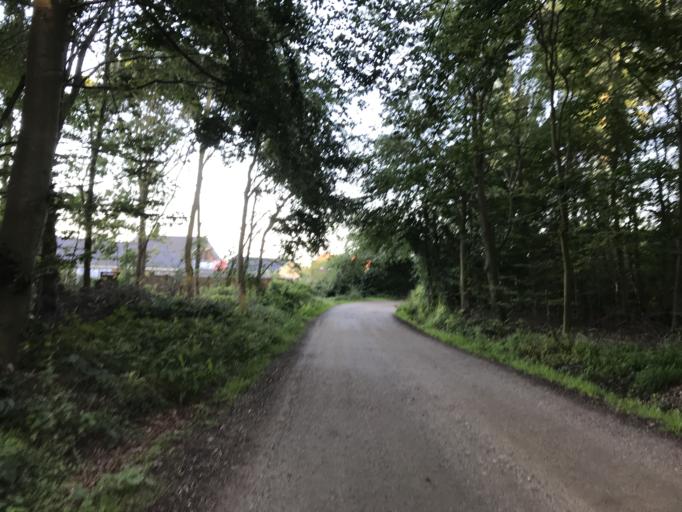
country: DK
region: South Denmark
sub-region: Middelfart Kommune
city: Middelfart
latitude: 55.4997
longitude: 9.7144
